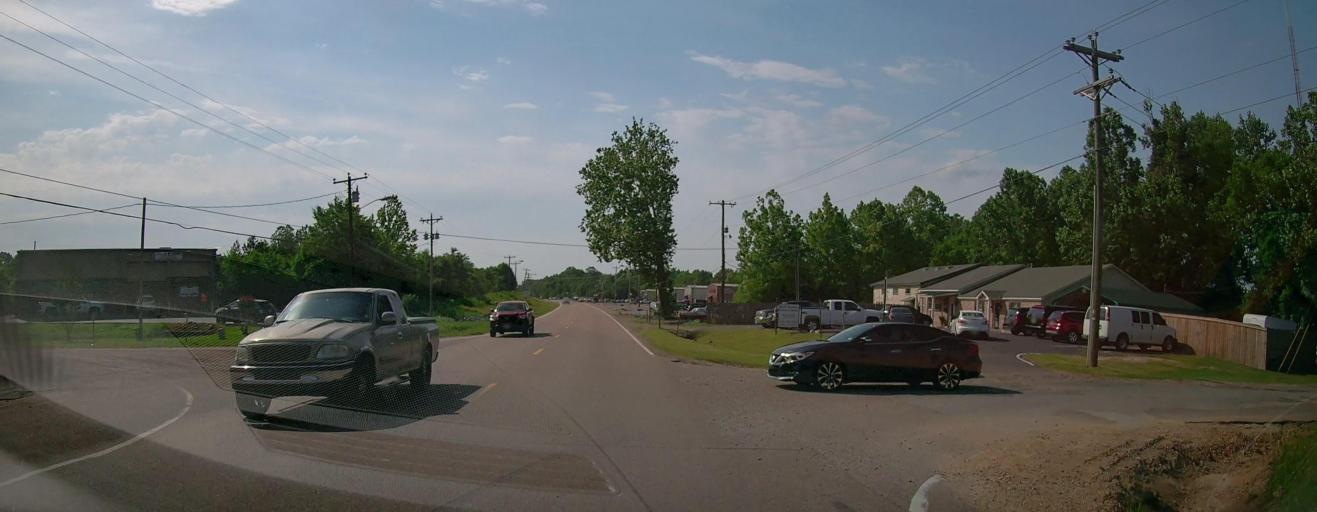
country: US
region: Mississippi
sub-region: De Soto County
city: Olive Branch
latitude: 34.9879
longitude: -89.8630
